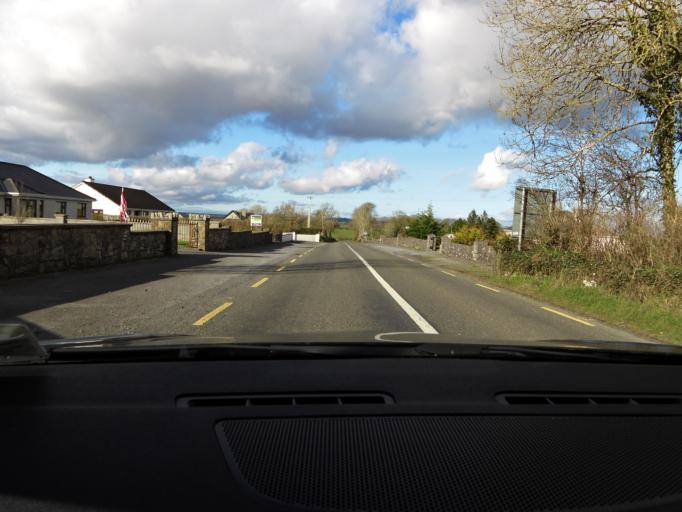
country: IE
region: Connaught
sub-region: Roscommon
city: Castlerea
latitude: 53.6846
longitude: -8.4836
